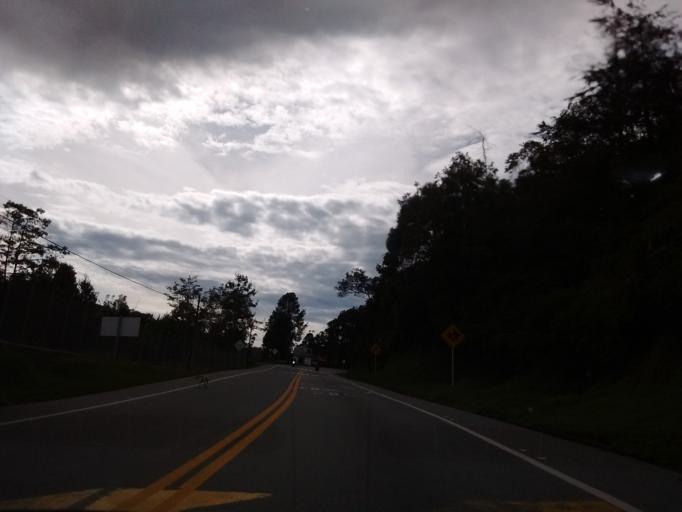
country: CO
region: Antioquia
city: Santuario
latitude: 6.1091
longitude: -75.2284
